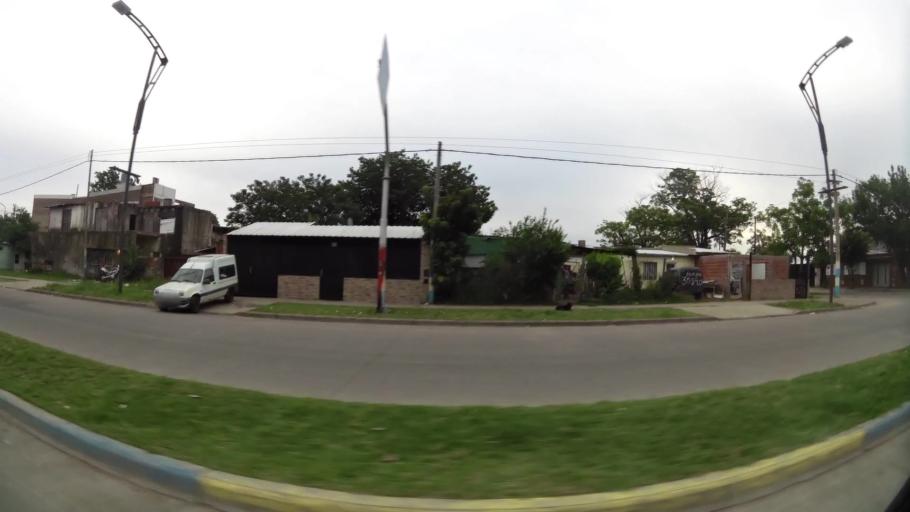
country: AR
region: Santa Fe
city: Granadero Baigorria
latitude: -32.9007
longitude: -60.7055
